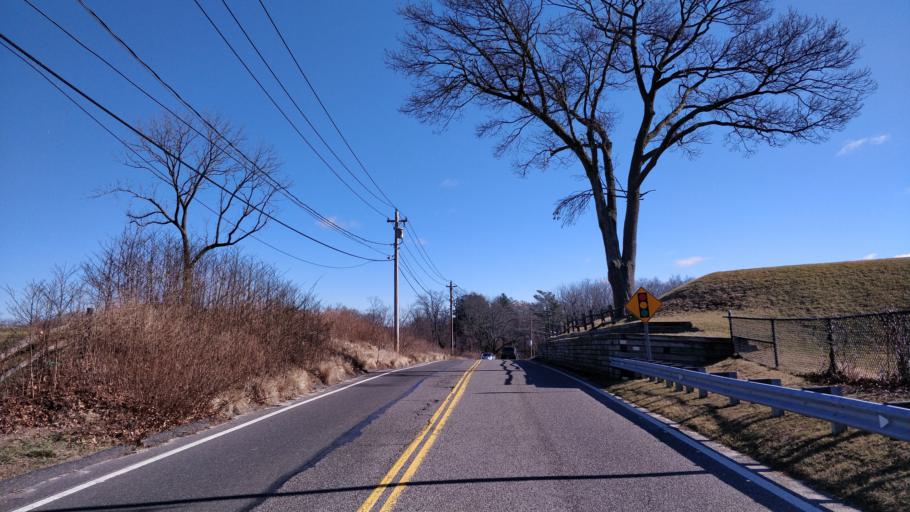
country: US
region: New York
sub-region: Suffolk County
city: Setauket-East Setauket
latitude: 40.9225
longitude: -73.1154
